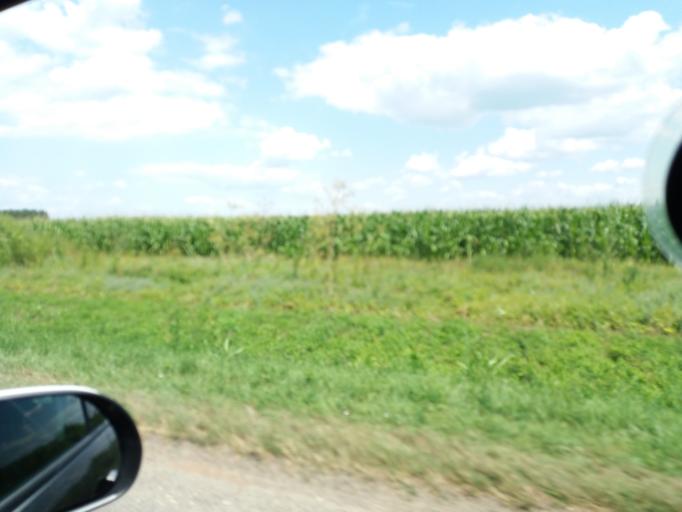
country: RS
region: Autonomna Pokrajina Vojvodina
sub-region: Sremski Okrug
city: Pecinci
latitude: 44.8577
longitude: 19.9603
